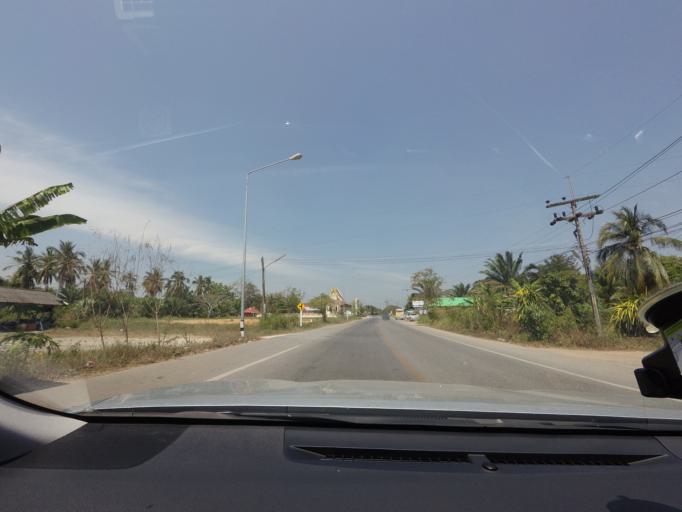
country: TH
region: Surat Thani
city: Tha Chang
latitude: 9.2028
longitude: 99.2429
